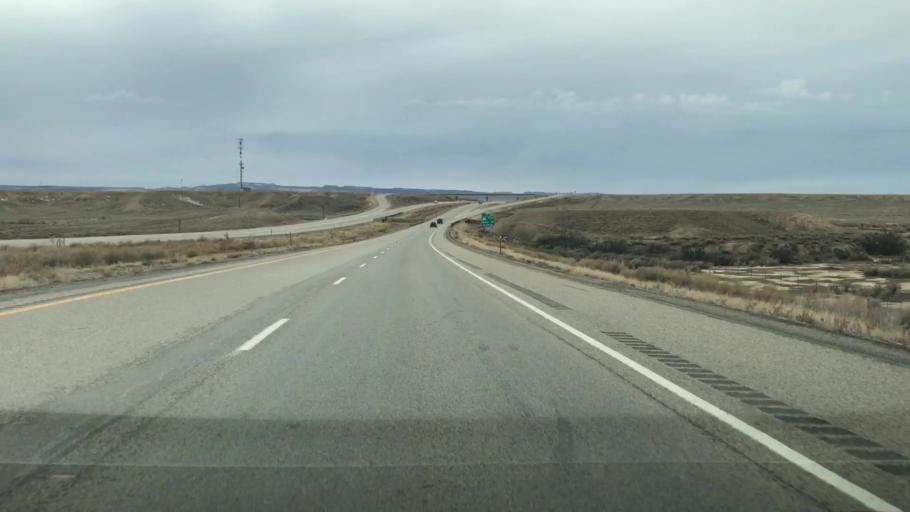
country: US
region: Utah
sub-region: Grand County
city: Moab
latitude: 38.9446
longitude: -109.3999
